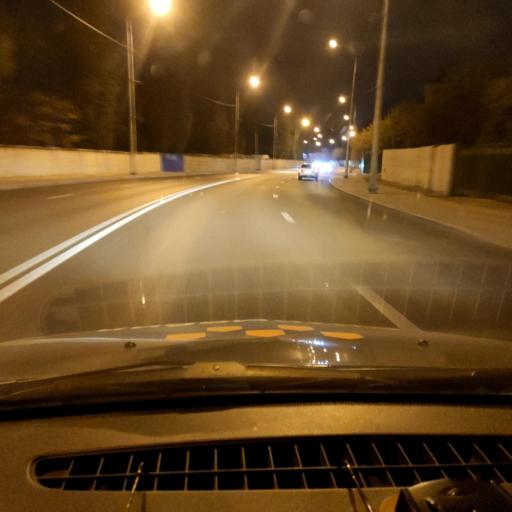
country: RU
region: Voronezj
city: Voronezh
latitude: 51.6878
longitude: 39.2311
